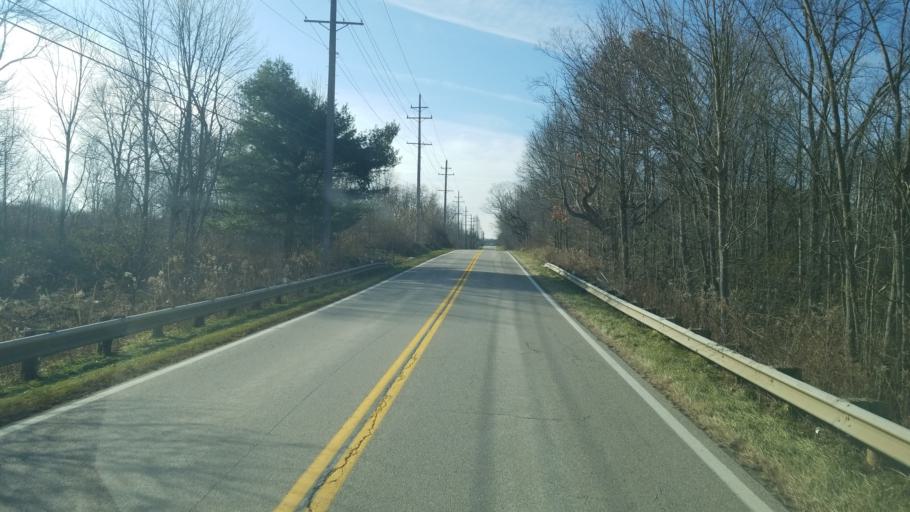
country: US
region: Ohio
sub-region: Ashtabula County
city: Jefferson
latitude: 41.7315
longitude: -80.8063
